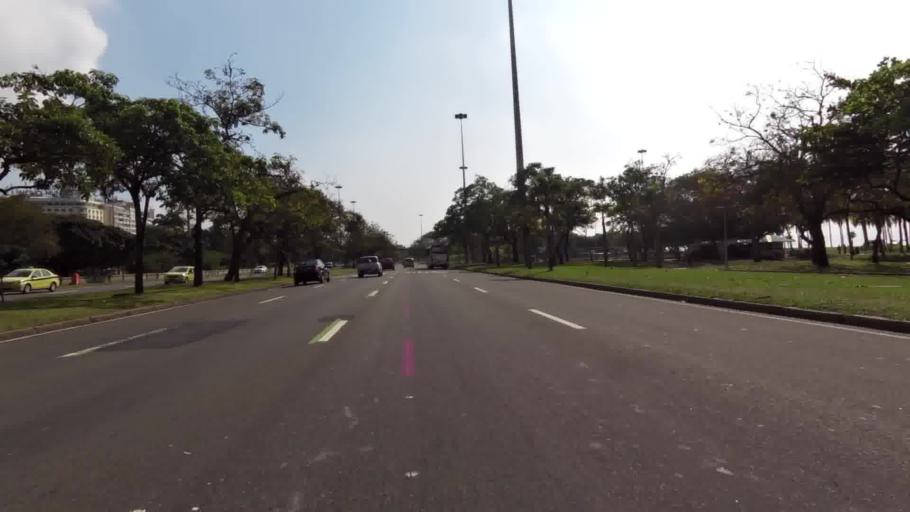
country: BR
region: Rio de Janeiro
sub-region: Rio De Janeiro
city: Rio de Janeiro
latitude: -22.9286
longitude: -43.1723
